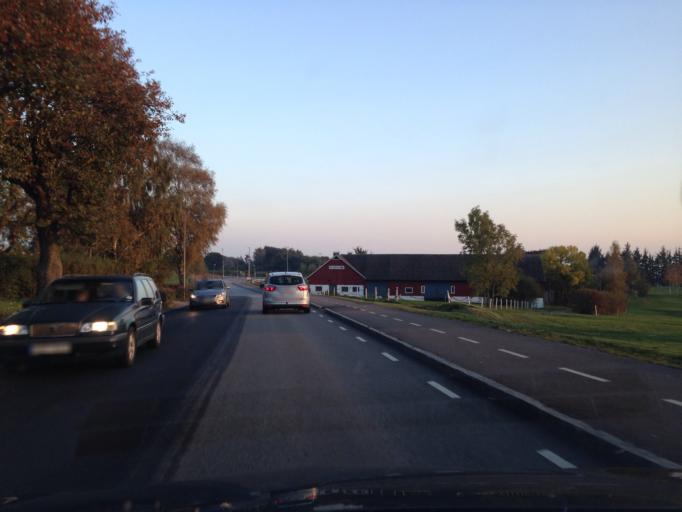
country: SE
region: Skane
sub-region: Bastads Kommun
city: Forslov
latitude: 56.3693
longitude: 12.7954
